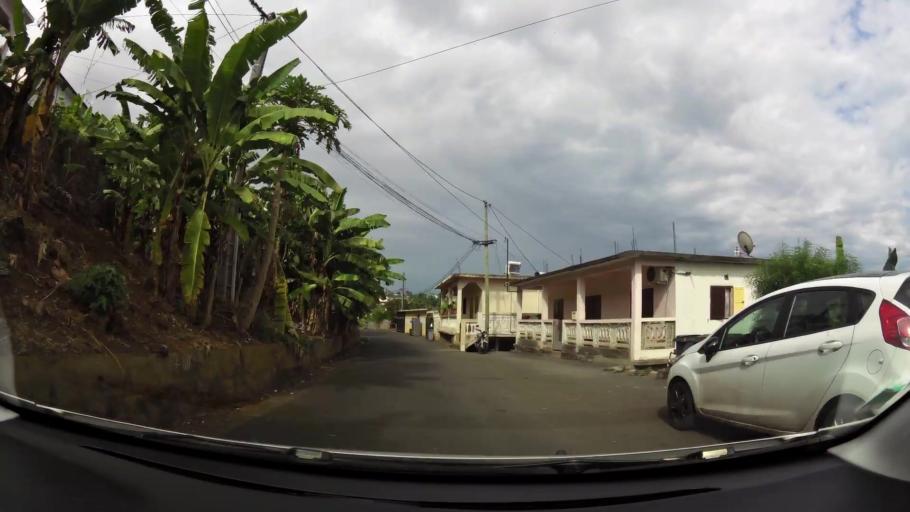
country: YT
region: Sada
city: Sada
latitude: -12.8472
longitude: 45.1022
